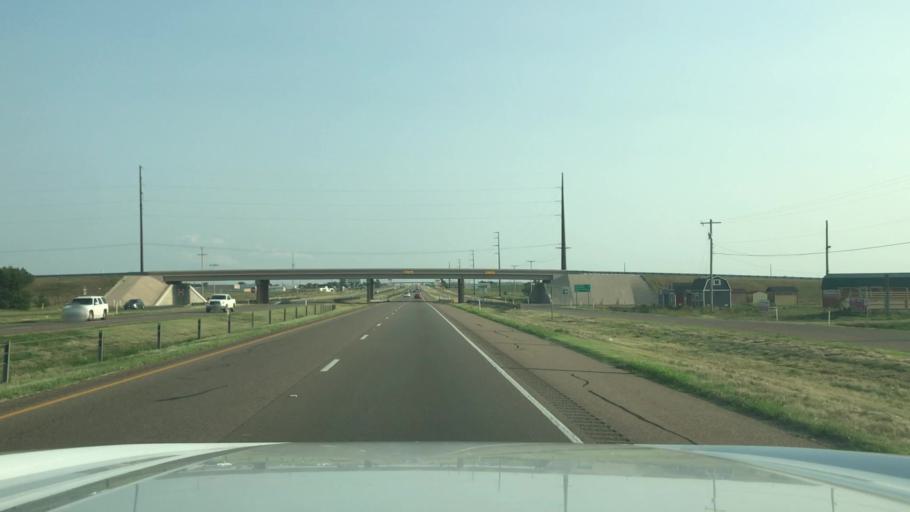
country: US
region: Texas
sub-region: Randall County
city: Canyon
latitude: 35.0595
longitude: -101.9194
